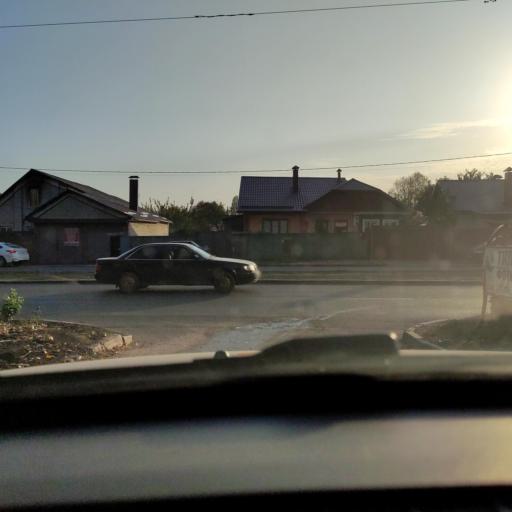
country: RU
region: Voronezj
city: Voronezh
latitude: 51.6353
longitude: 39.1735
